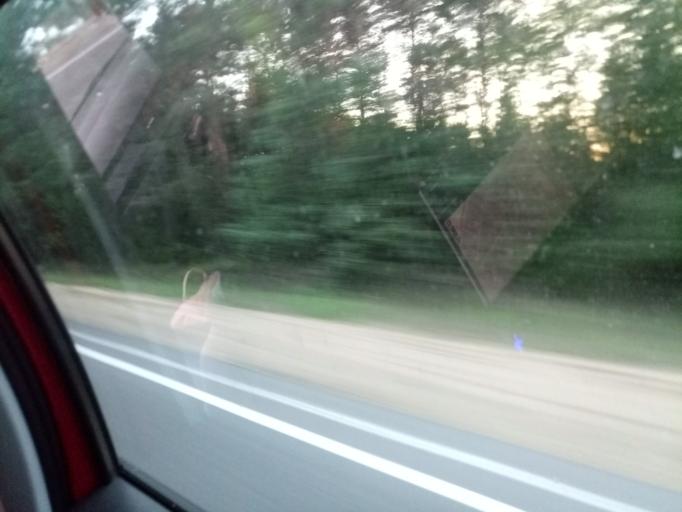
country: RU
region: Moskovskaya
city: Noginsk-9
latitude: 56.0754
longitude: 38.5697
